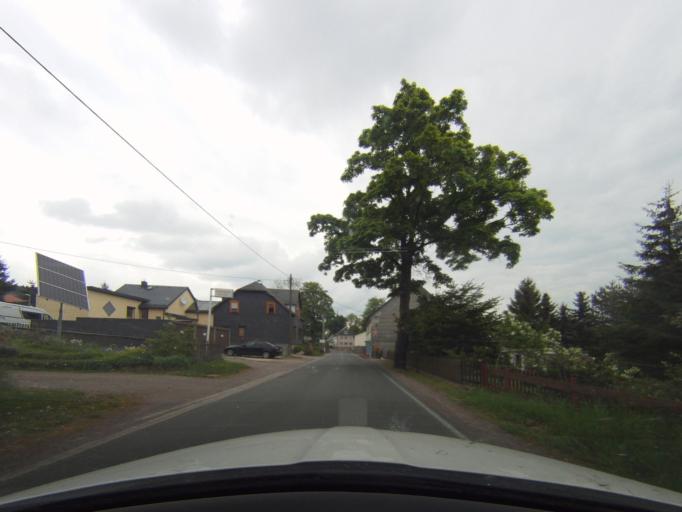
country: DE
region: Thuringia
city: Gillersdorf
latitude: 50.6054
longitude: 11.0155
